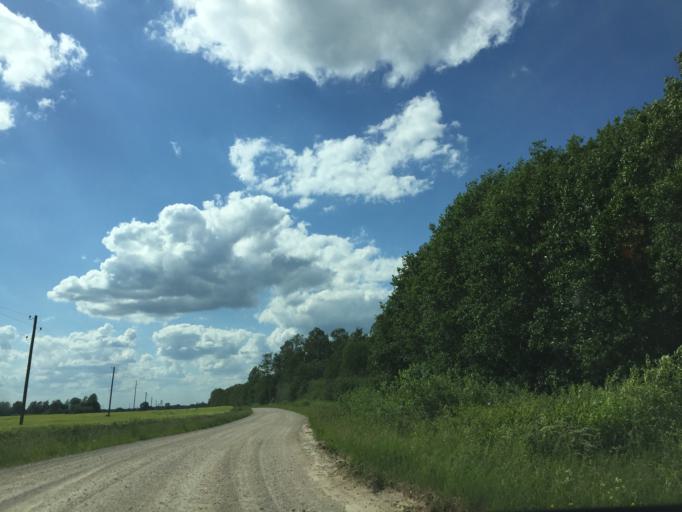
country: LV
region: Tukuma Rajons
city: Tukums
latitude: 56.8944
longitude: 23.0920
